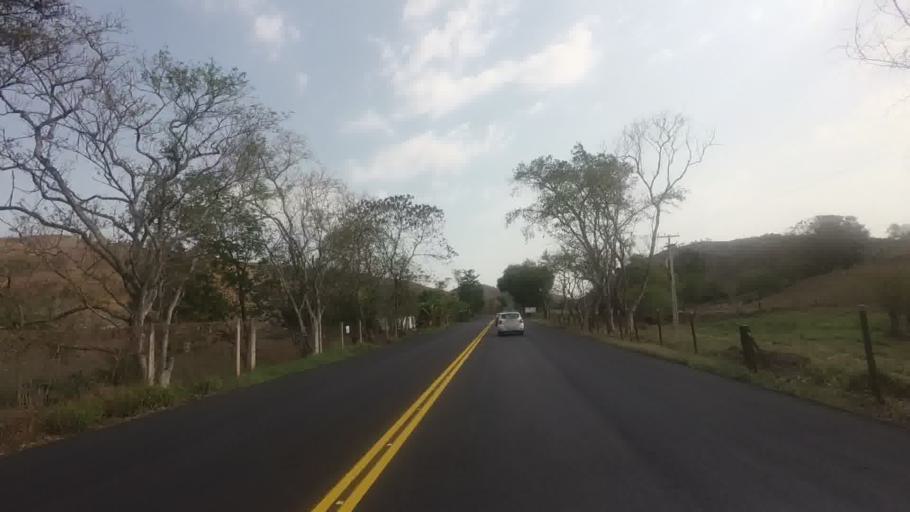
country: BR
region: Rio de Janeiro
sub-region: Bom Jesus Do Itabapoana
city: Bom Jesus do Itabapoana
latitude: -21.2248
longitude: -41.7429
